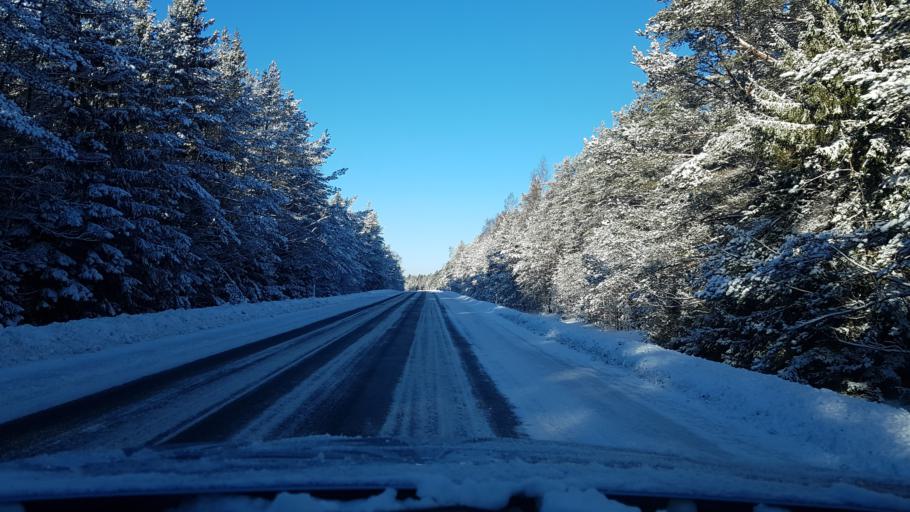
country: EE
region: Hiiumaa
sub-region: Kaerdla linn
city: Kardla
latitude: 58.9861
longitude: 22.7972
